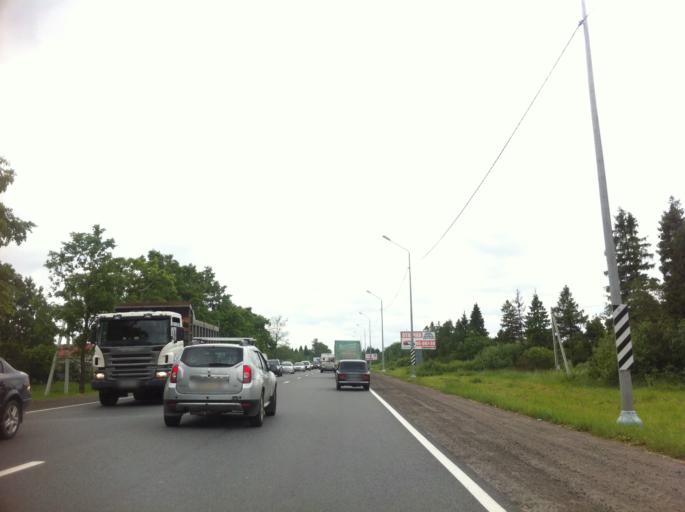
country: RU
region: Leningrad
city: Maloye Verevo
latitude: 59.6582
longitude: 30.2198
